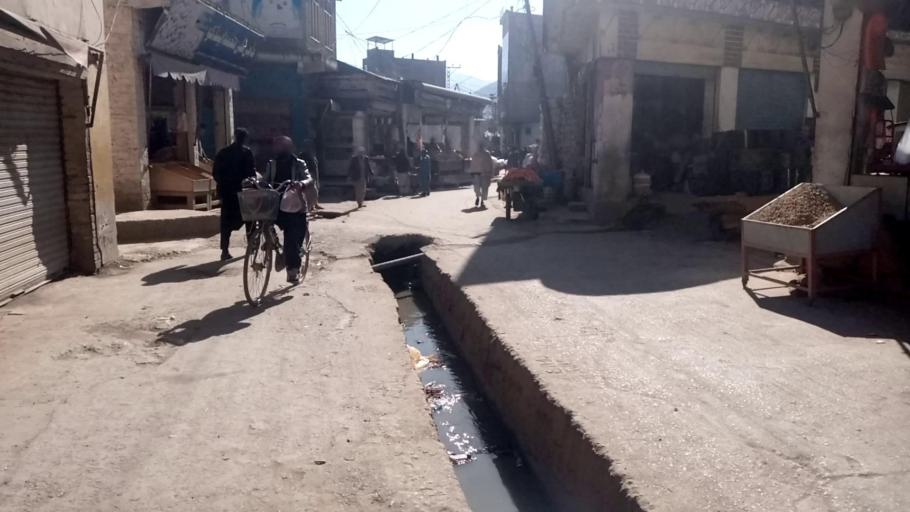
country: PK
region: Khyber Pakhtunkhwa
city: Mingora
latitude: 34.7807
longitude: 72.3597
